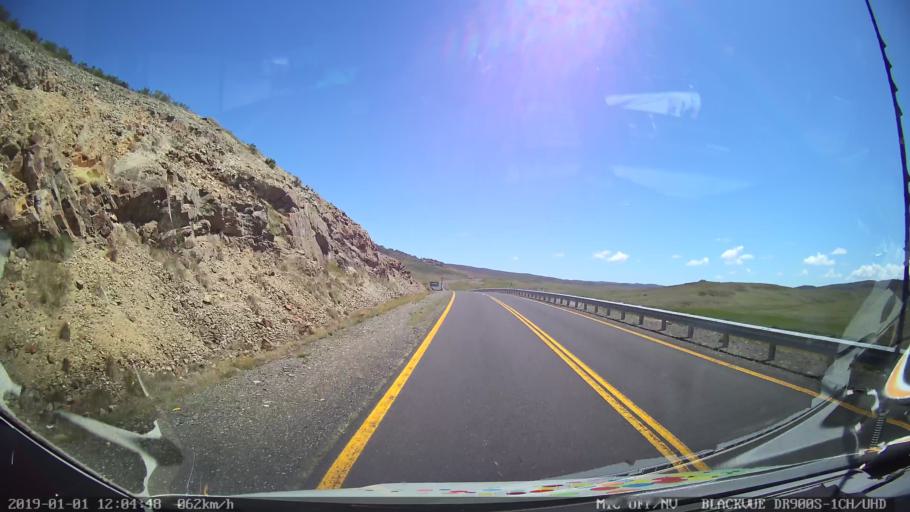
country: AU
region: New South Wales
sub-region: Snowy River
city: Jindabyne
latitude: -35.8638
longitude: 148.4959
